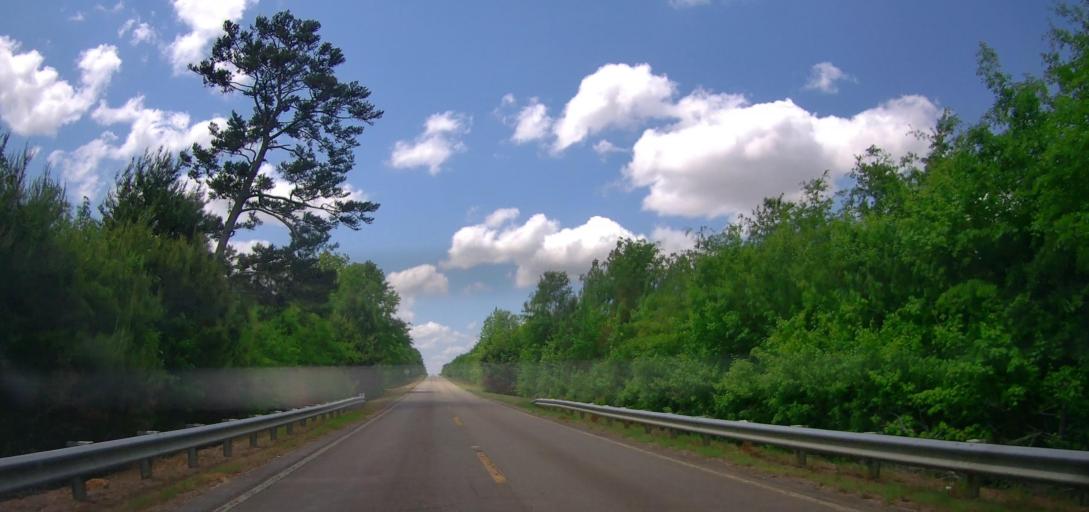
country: US
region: Georgia
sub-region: Dodge County
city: Chester
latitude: 32.5346
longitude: -83.2000
